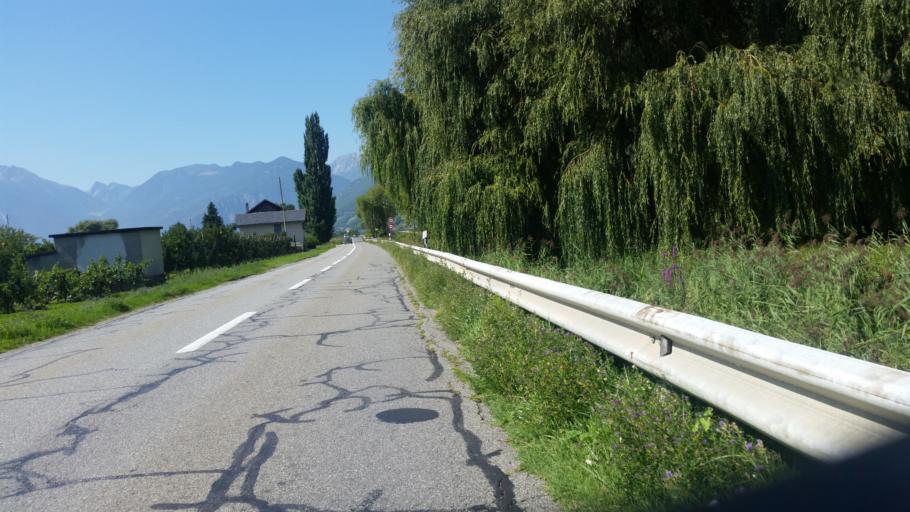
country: CH
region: Valais
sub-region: Martigny District
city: Saxon
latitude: 46.1561
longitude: 7.1546
